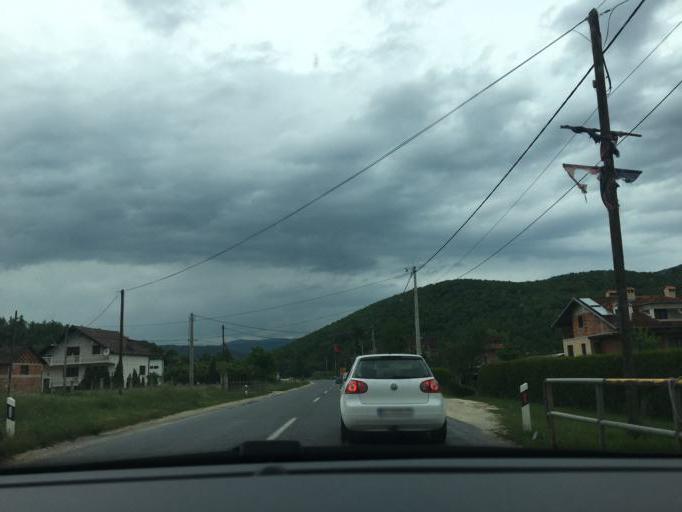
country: MK
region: Kicevo
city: Zajas
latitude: 41.5693
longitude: 20.9571
